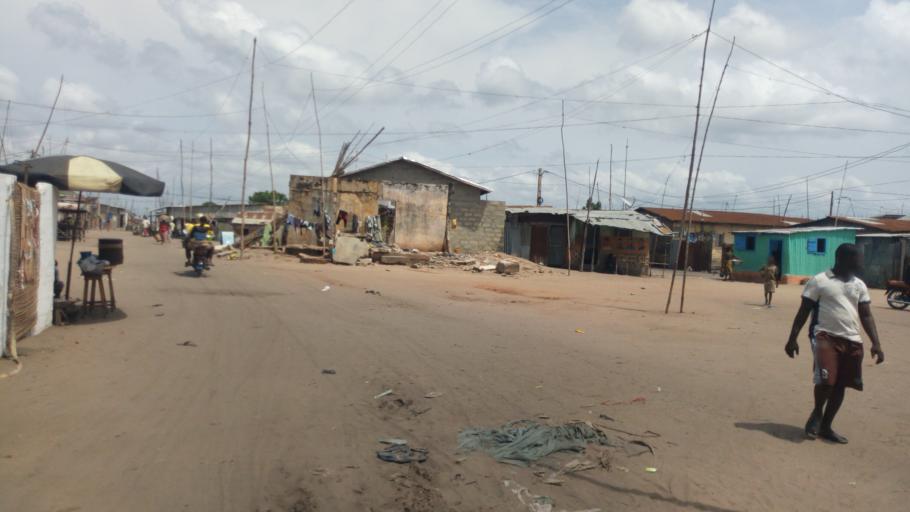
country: BJ
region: Littoral
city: Cotonou
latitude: 6.3889
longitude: 2.4319
